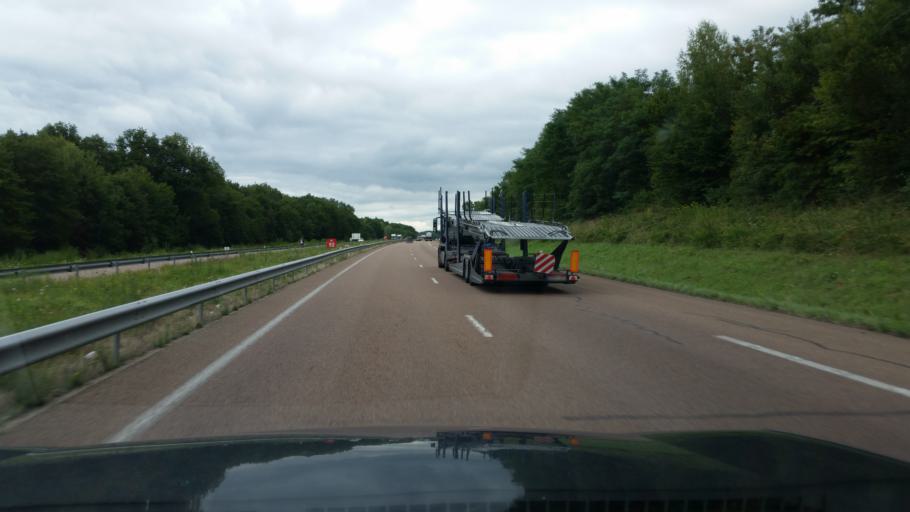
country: FR
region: Franche-Comte
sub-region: Departement du Jura
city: Bletterans
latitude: 46.6768
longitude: 5.4334
